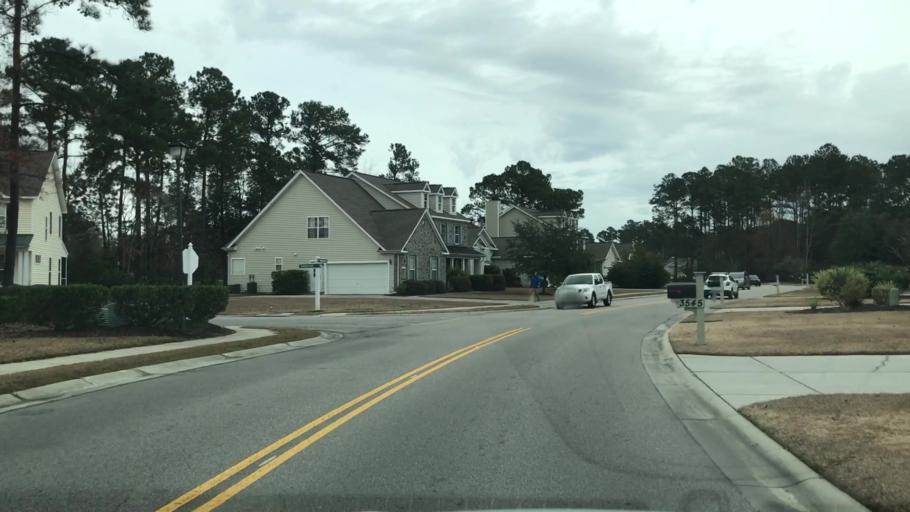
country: US
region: South Carolina
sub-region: Horry County
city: Forestbrook
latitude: 33.7107
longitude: -78.9458
